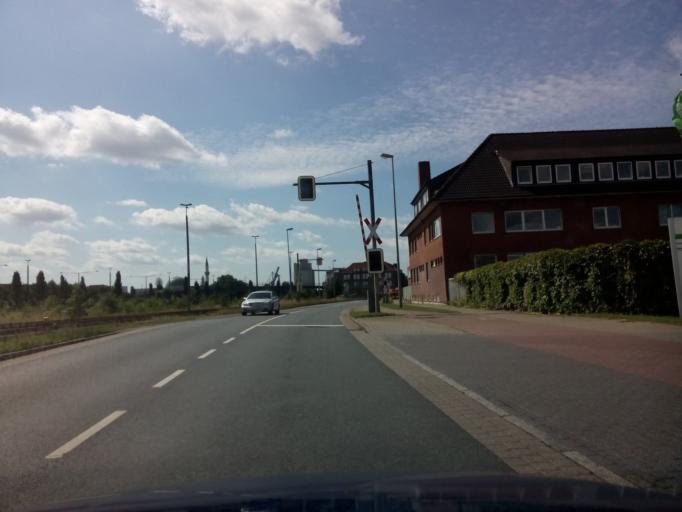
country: DE
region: Lower Saxony
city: Ritterhude
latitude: 53.1183
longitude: 8.7516
